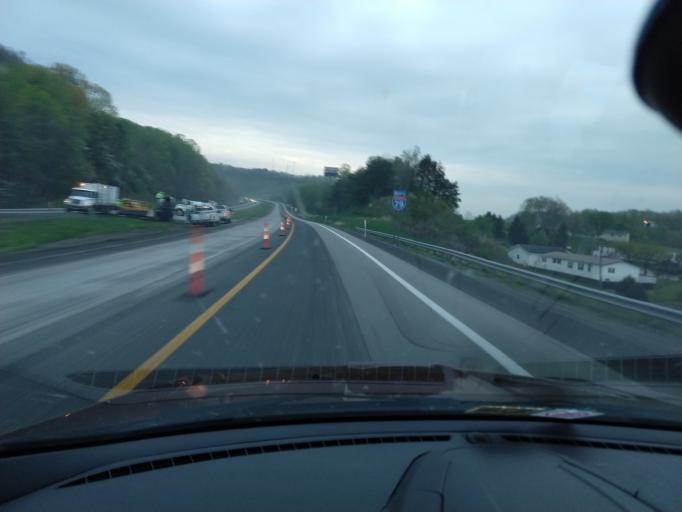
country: US
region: West Virginia
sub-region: Braxton County
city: Sutton
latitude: 38.7119
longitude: -80.6585
